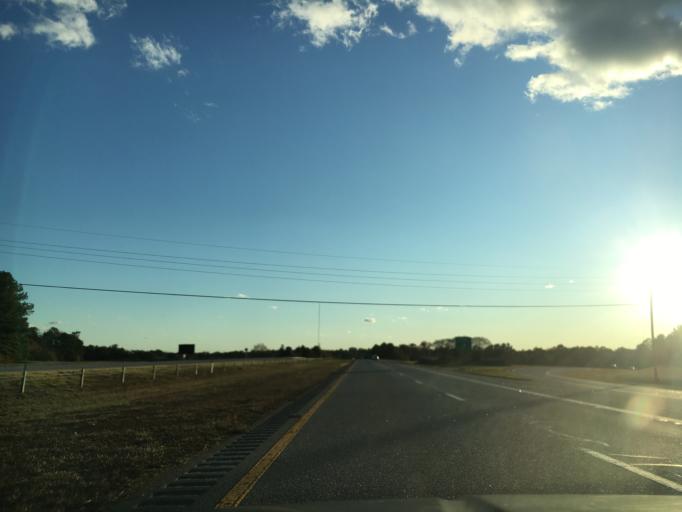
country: US
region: South Carolina
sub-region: Richland County
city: Dentsville
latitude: 34.0594
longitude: -80.9890
